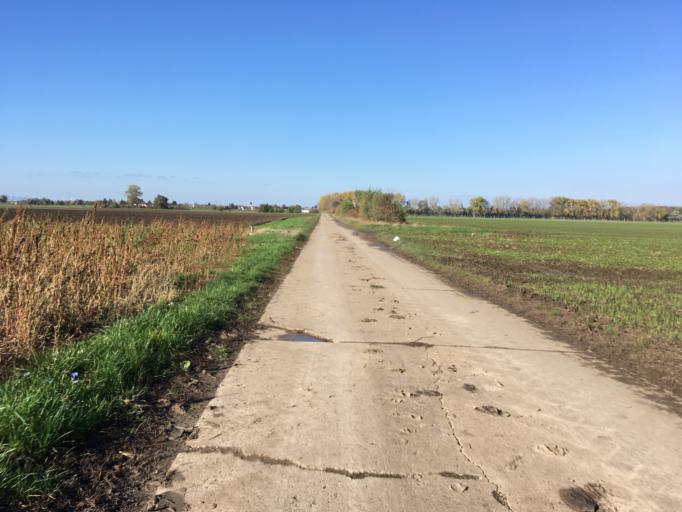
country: DE
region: Hesse
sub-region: Regierungsbezirk Darmstadt
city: Burstadt
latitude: 49.6597
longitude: 8.4696
